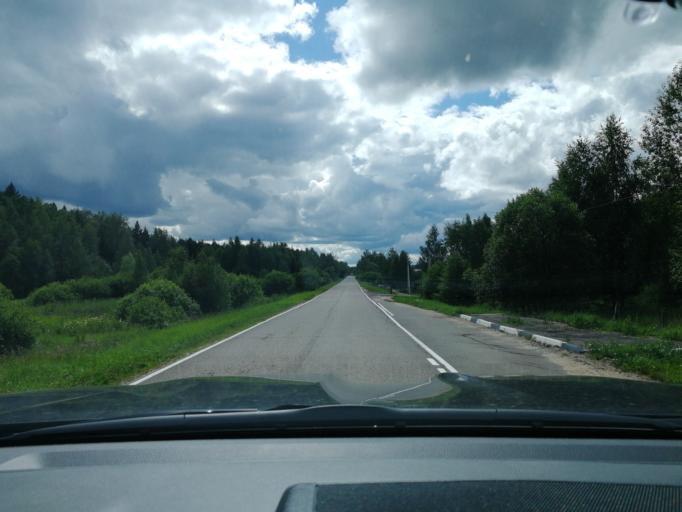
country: RU
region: Moskovskaya
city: Proletarskiy
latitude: 55.0154
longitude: 37.4909
